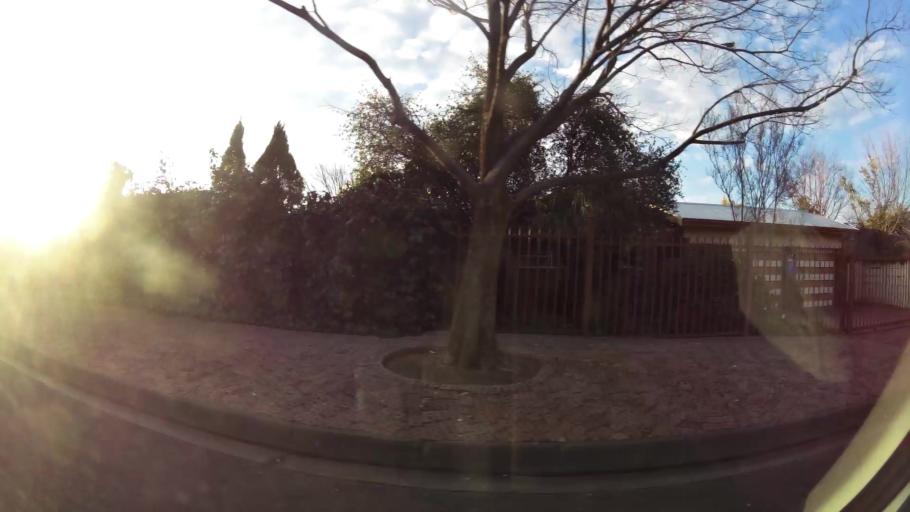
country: ZA
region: Orange Free State
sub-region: Mangaung Metropolitan Municipality
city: Bloemfontein
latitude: -29.1409
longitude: 26.1861
